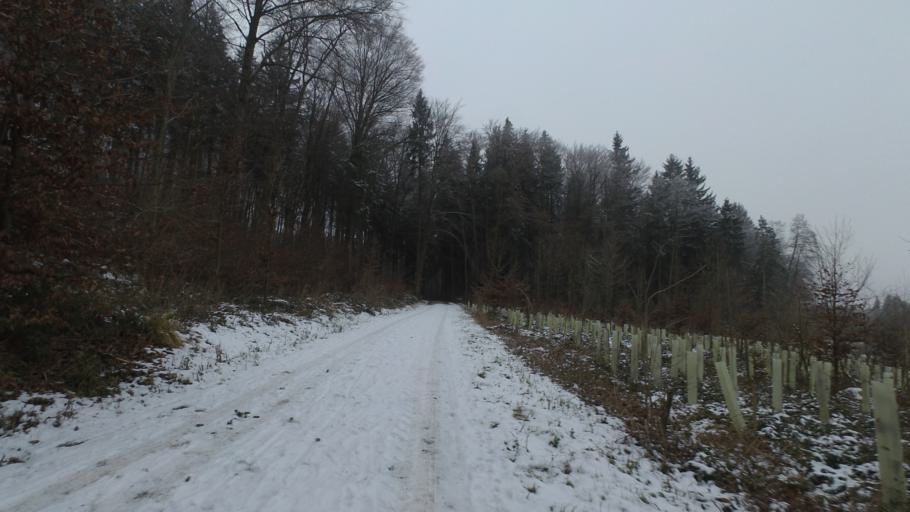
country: DE
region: Bavaria
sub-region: Upper Bavaria
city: Nussdorf
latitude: 47.9009
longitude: 12.5861
